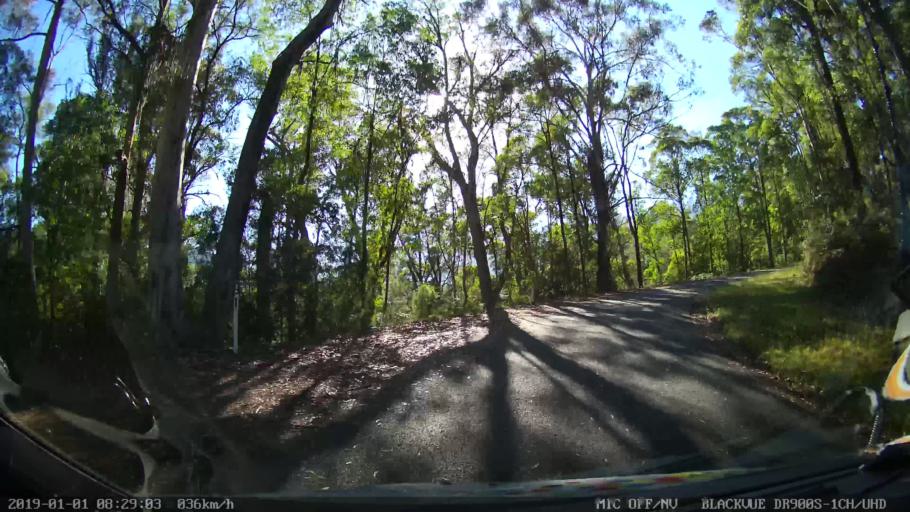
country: AU
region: New South Wales
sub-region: Snowy River
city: Jindabyne
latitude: -36.3731
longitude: 148.1919
